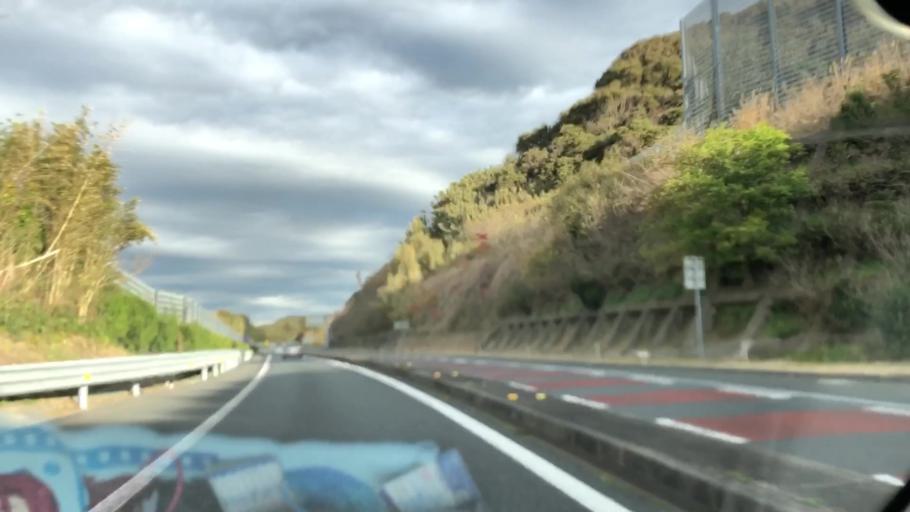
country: JP
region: Chiba
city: Tateyama
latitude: 35.0443
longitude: 139.8533
